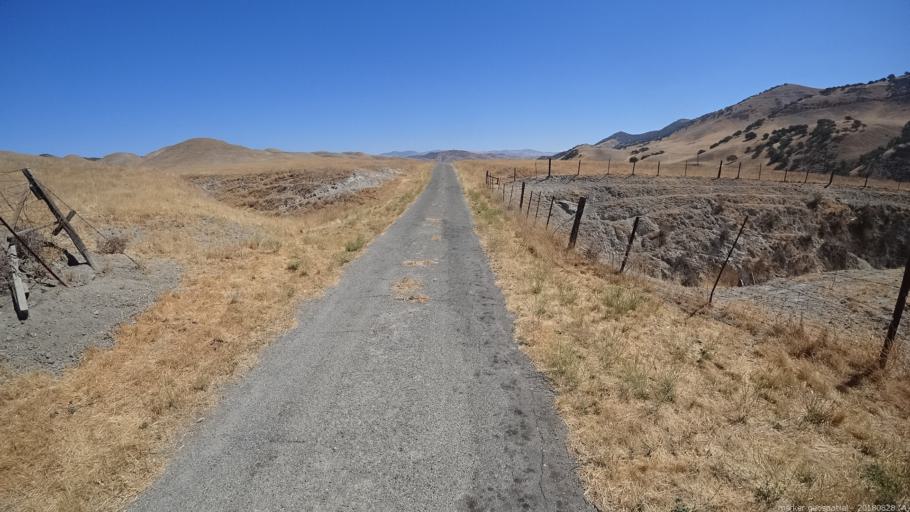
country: US
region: California
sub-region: San Luis Obispo County
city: San Miguel
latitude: 36.0545
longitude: -120.8100
